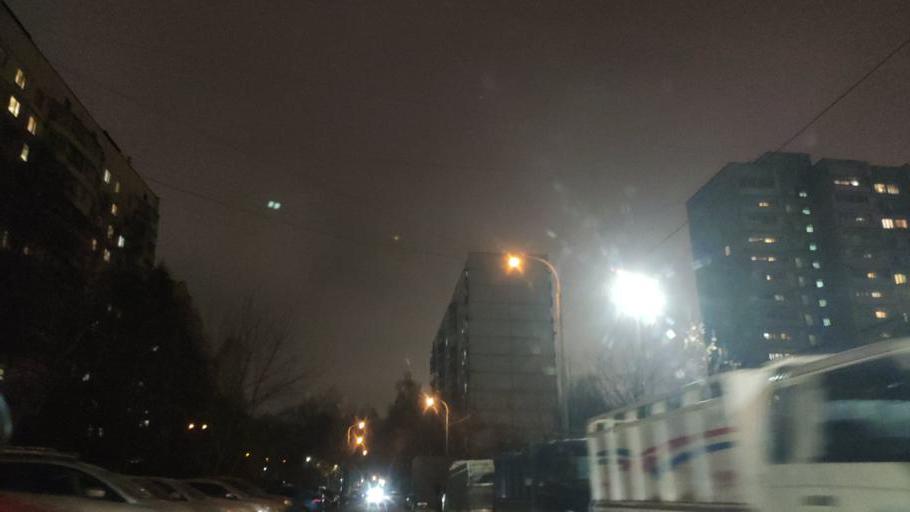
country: RU
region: Moscow
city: Tyoply Stan
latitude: 55.6205
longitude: 37.4957
